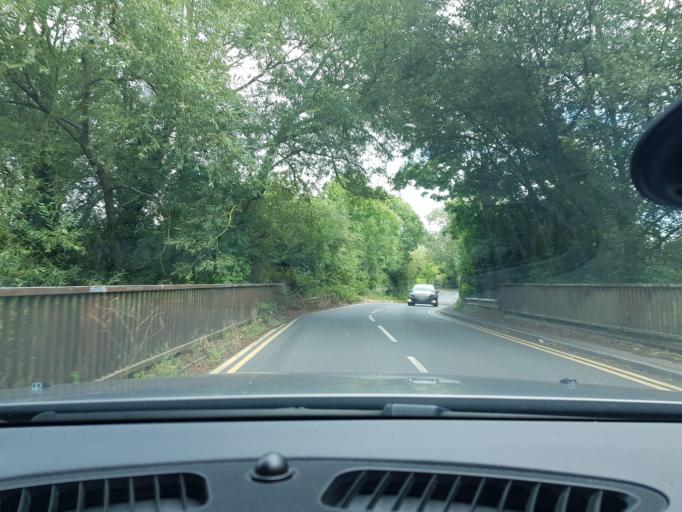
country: GB
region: England
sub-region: Buckinghamshire
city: Iver
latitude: 51.4873
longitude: -0.4895
